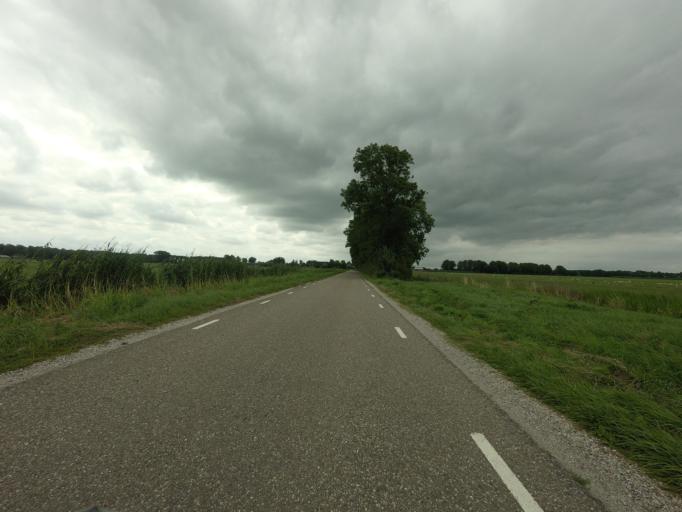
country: NL
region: South Holland
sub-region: Gemeente Giessenlanden
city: Giessenburg
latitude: 51.8962
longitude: 4.9023
